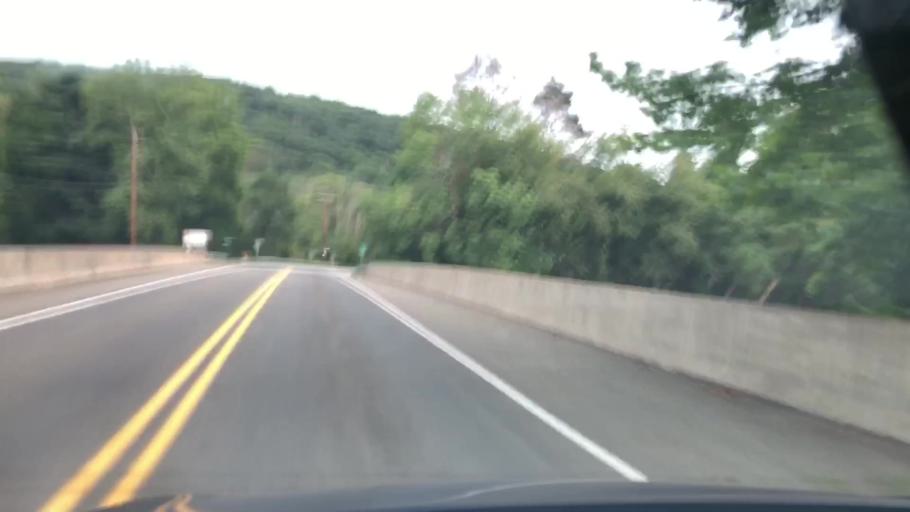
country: US
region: Pennsylvania
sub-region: Venango County
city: Hasson Heights
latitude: 41.4822
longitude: -79.6956
